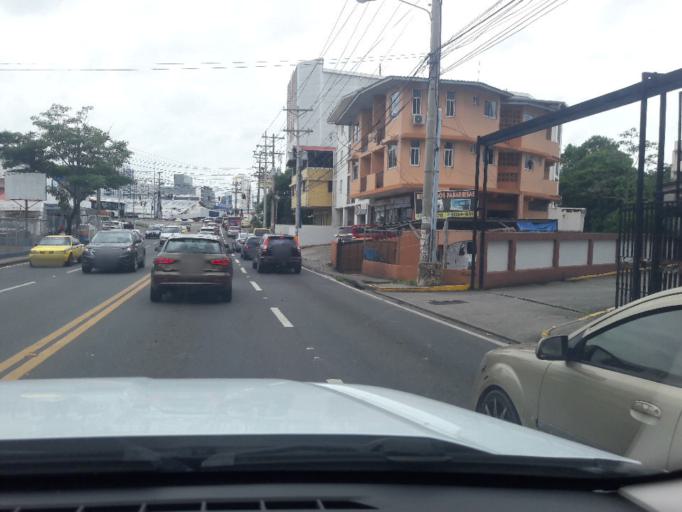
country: PA
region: Panama
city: Panama
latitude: 9.0074
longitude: -79.5206
